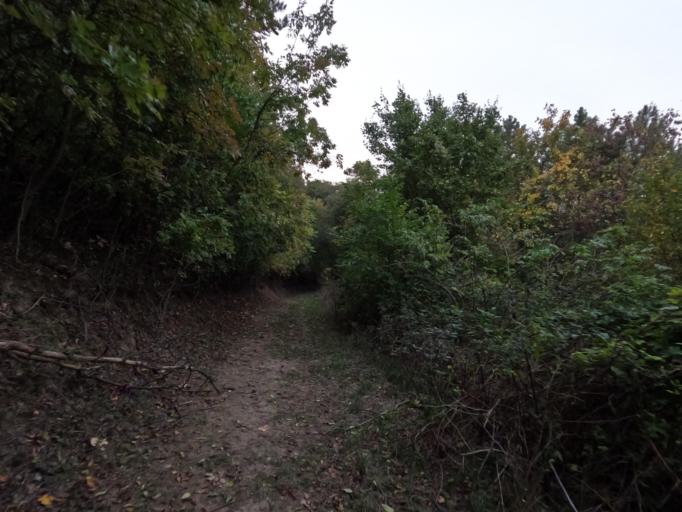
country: HU
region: Tolna
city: Szentgalpuszta
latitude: 46.3528
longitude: 18.6125
